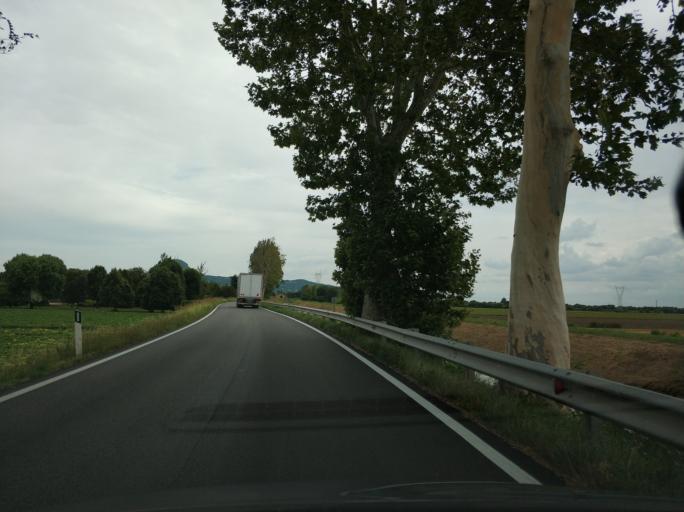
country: IT
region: Veneto
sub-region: Provincia di Padova
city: Lozzo Atestino
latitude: 45.2693
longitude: 11.5921
